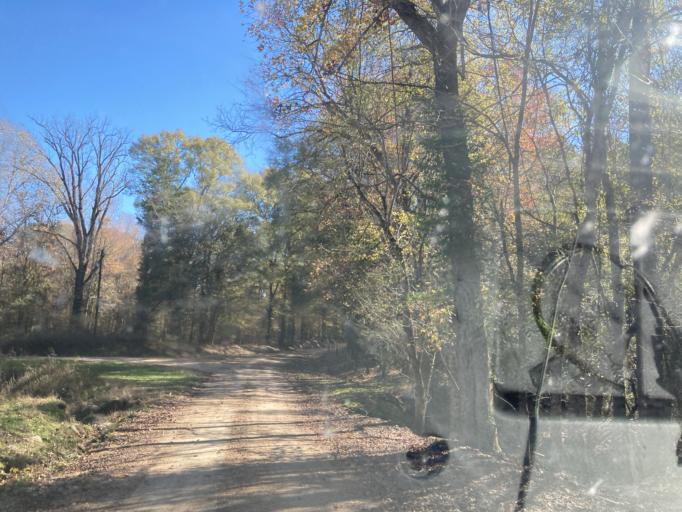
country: US
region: Mississippi
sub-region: Hinds County
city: Lynchburg
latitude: 32.5533
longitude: -90.5004
